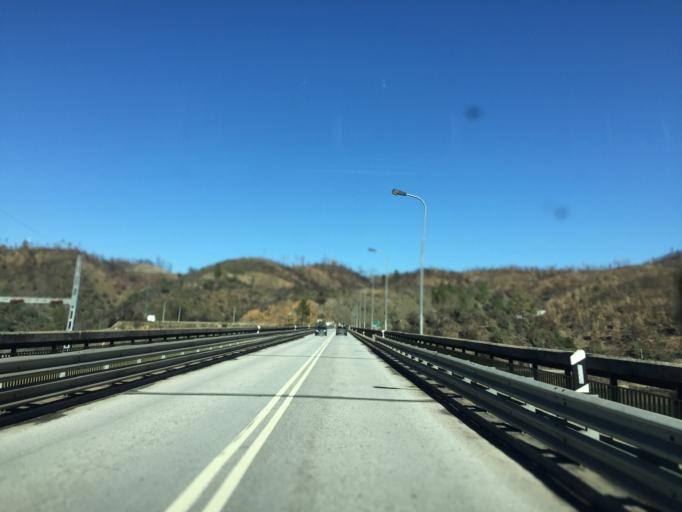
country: PT
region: Portalegre
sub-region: Gaviao
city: Gaviao
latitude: 39.5425
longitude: -7.8025
